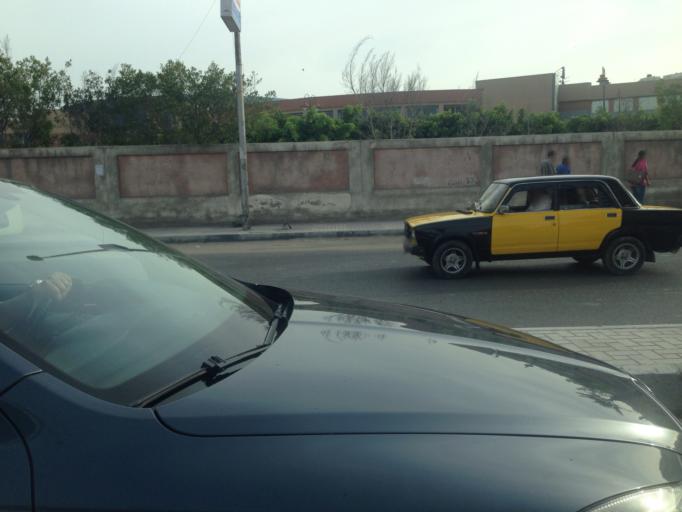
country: EG
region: Alexandria
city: Alexandria
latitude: 31.2075
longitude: 29.9658
